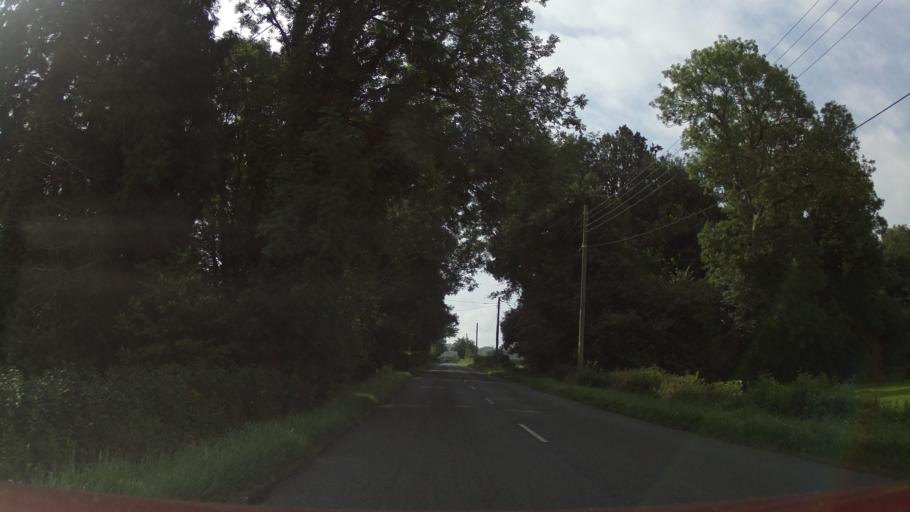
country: GB
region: England
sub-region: Bath and North East Somerset
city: East Harptree
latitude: 51.2983
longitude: -2.6015
